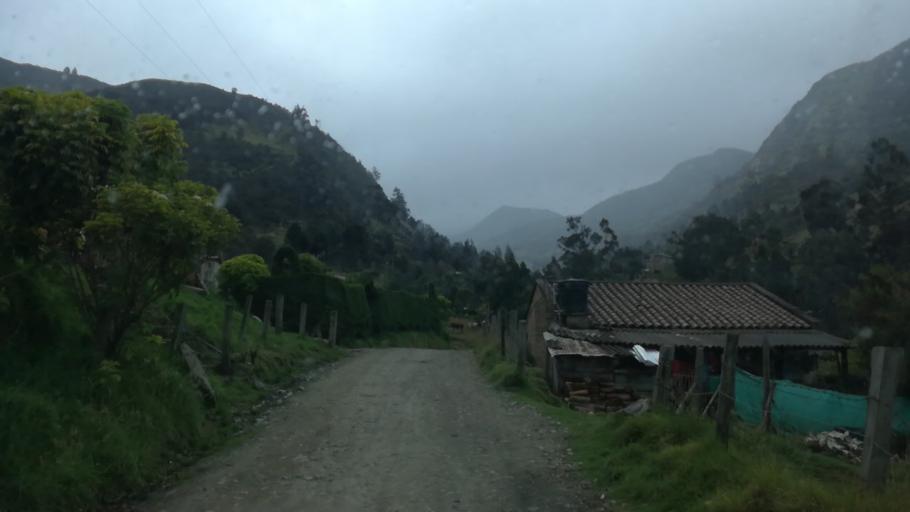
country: CO
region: Boyaca
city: Socha Viejo
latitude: 5.9382
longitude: -72.6904
